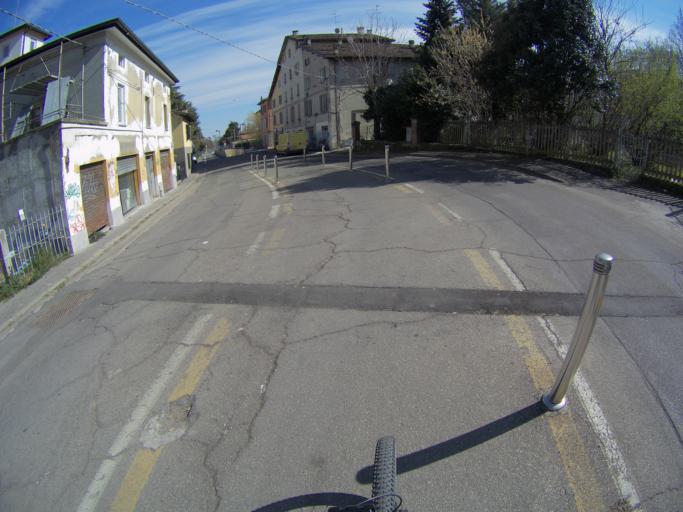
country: IT
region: Emilia-Romagna
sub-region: Provincia di Reggio Emilia
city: Reggio nell'Emilia
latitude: 44.7019
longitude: 10.6376
